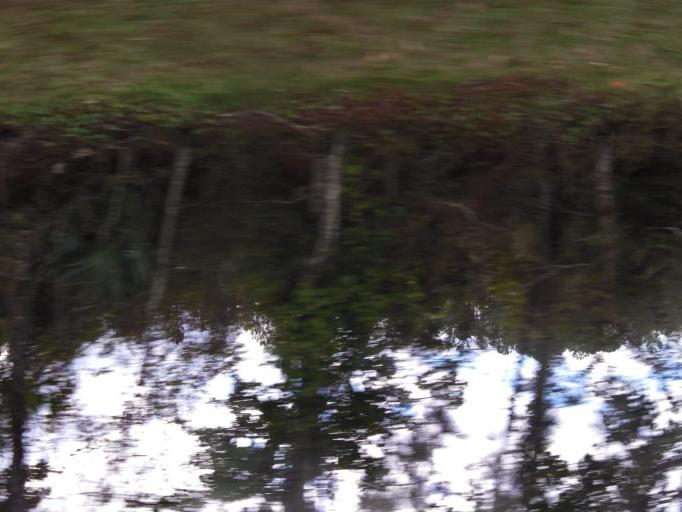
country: US
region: Florida
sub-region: Saint Johns County
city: Villano Beach
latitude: 30.0061
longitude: -81.4075
